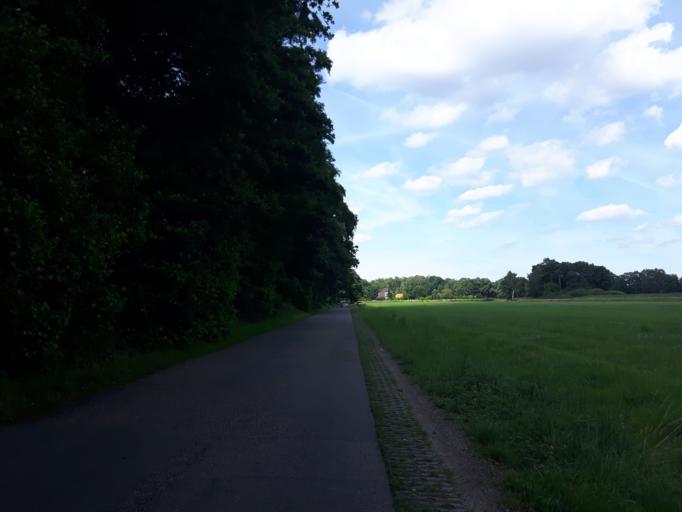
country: NL
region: Overijssel
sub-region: Gemeente Haaksbergen
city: Haaksbergen
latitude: 52.1845
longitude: 6.7751
